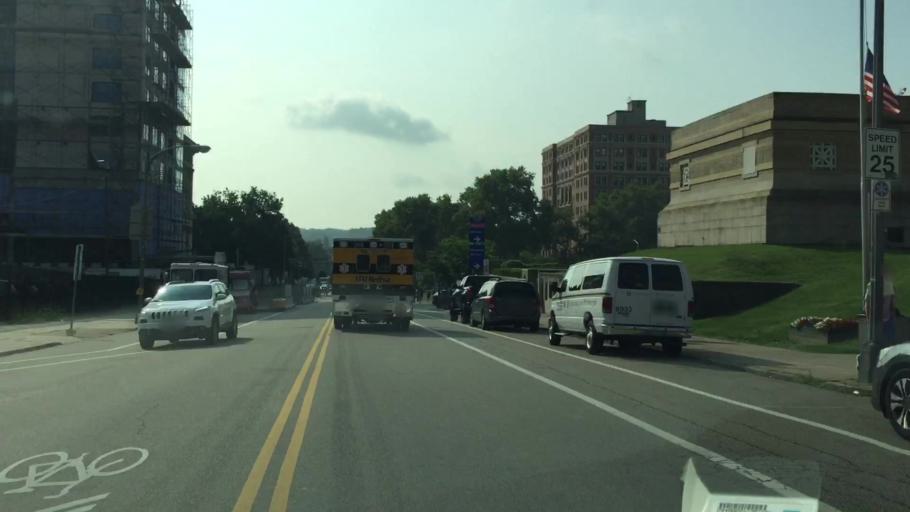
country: US
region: Pennsylvania
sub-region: Allegheny County
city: Bloomfield
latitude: 40.4455
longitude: -79.9562
